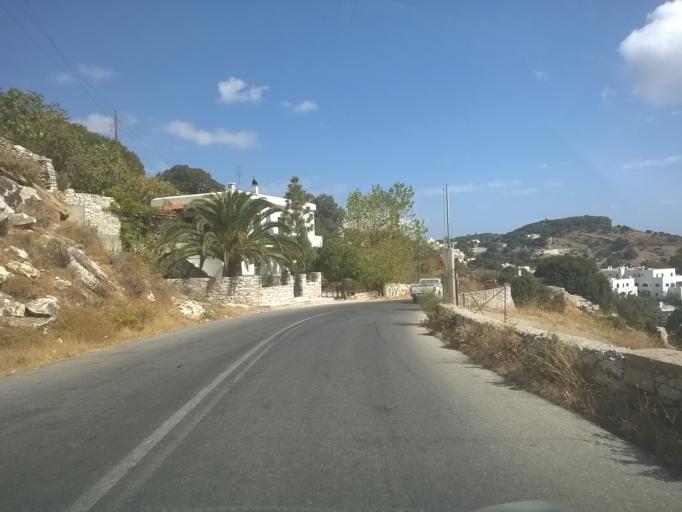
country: GR
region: South Aegean
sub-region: Nomos Kykladon
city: Filotion
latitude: 37.0666
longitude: 25.5153
